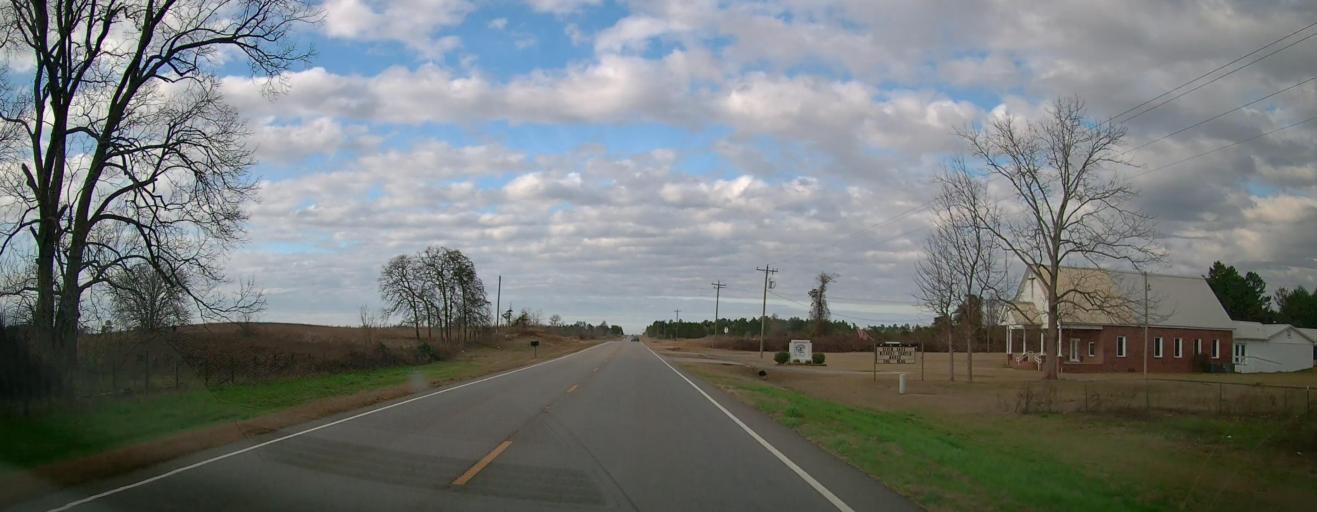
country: US
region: Georgia
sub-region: Marion County
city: Buena Vista
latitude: 32.4681
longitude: -84.5405
